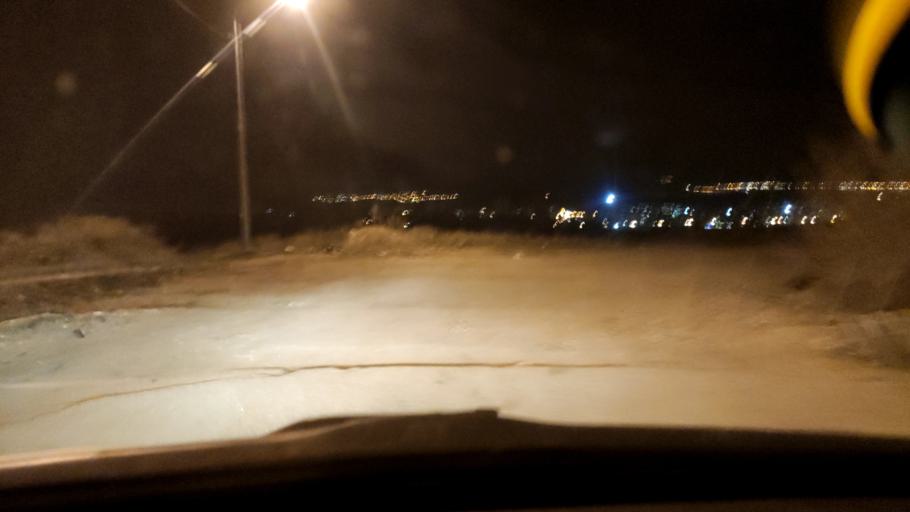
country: RU
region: Samara
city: Zhigulevsk
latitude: 53.4832
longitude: 49.5385
